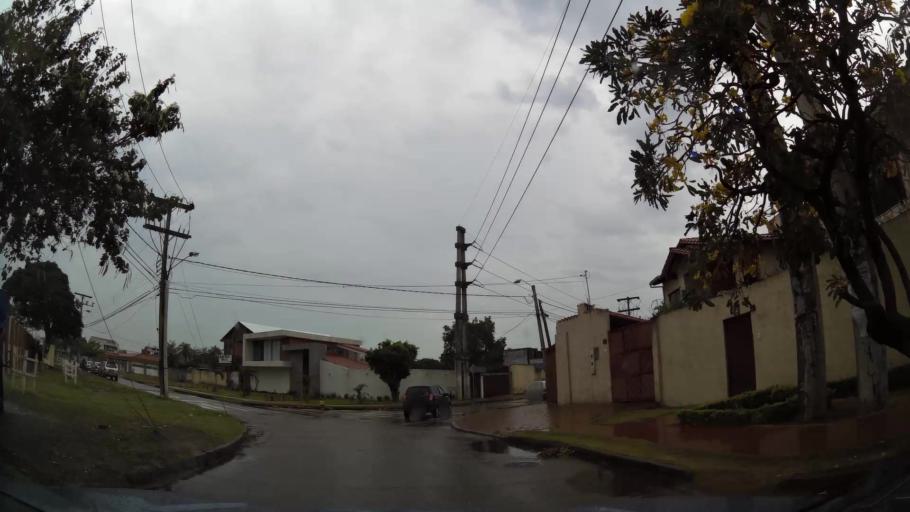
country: BO
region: Santa Cruz
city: Santa Cruz de la Sierra
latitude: -17.7838
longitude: -63.1518
